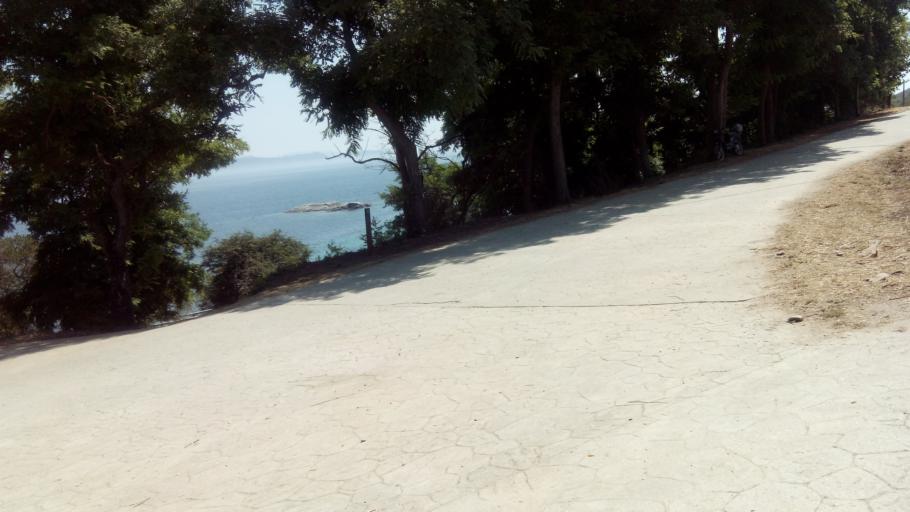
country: ES
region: Galicia
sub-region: Provincia de Pontevedra
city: Sanxenxo
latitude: 42.3763
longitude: -8.9330
